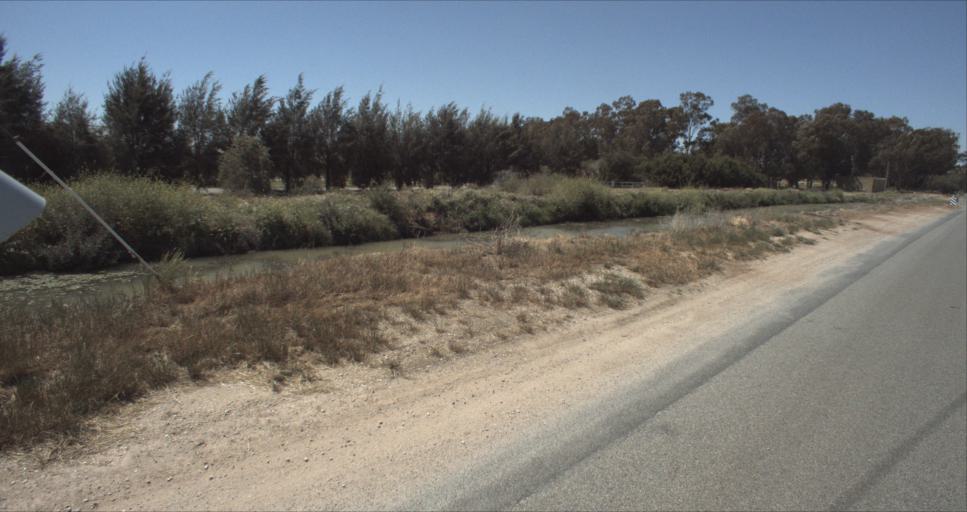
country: AU
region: New South Wales
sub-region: Leeton
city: Leeton
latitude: -34.5328
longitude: 146.3947
